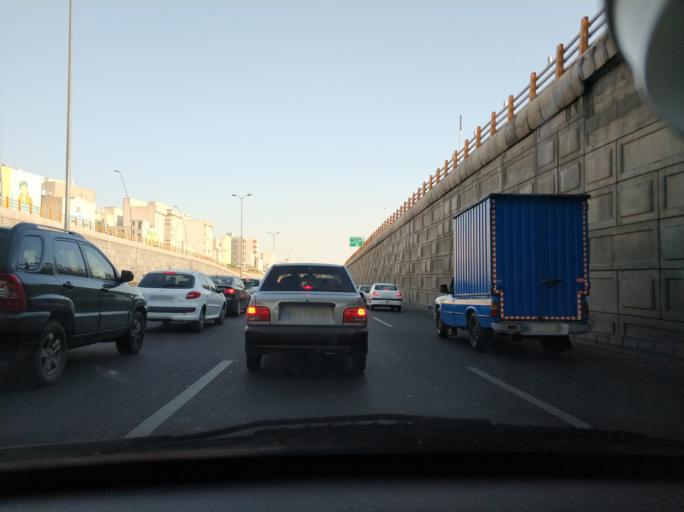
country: IR
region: Tehran
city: Tehran
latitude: 35.6938
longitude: 51.4566
